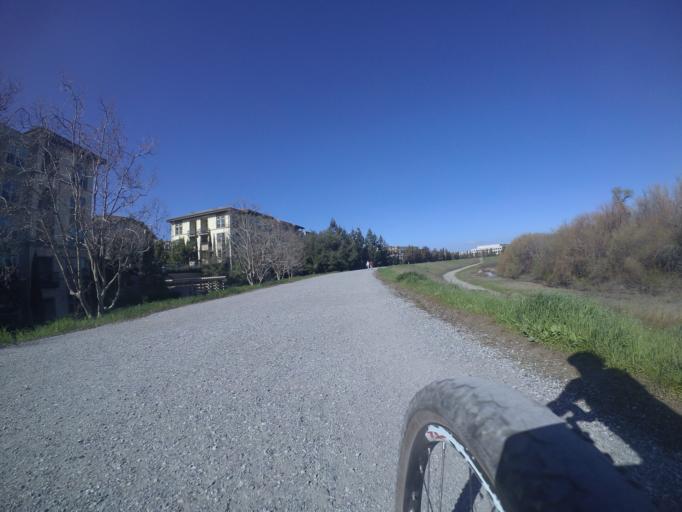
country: US
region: California
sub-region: Santa Clara County
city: Milpitas
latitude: 37.4048
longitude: -121.9237
